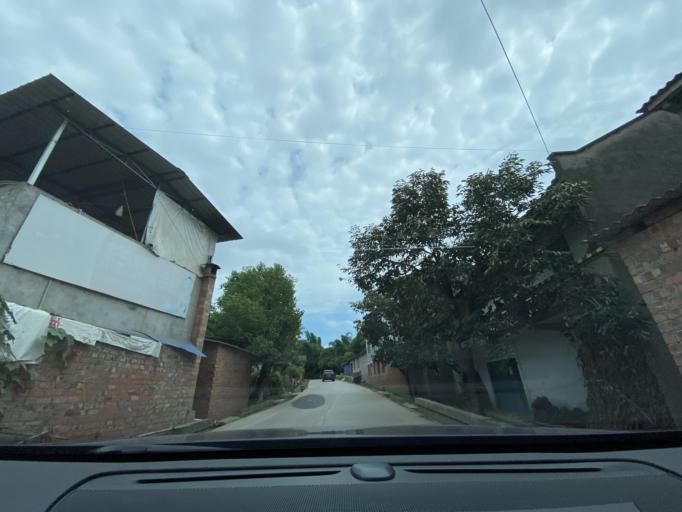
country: CN
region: Sichuan
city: Jiancheng
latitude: 30.4417
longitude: 104.5433
